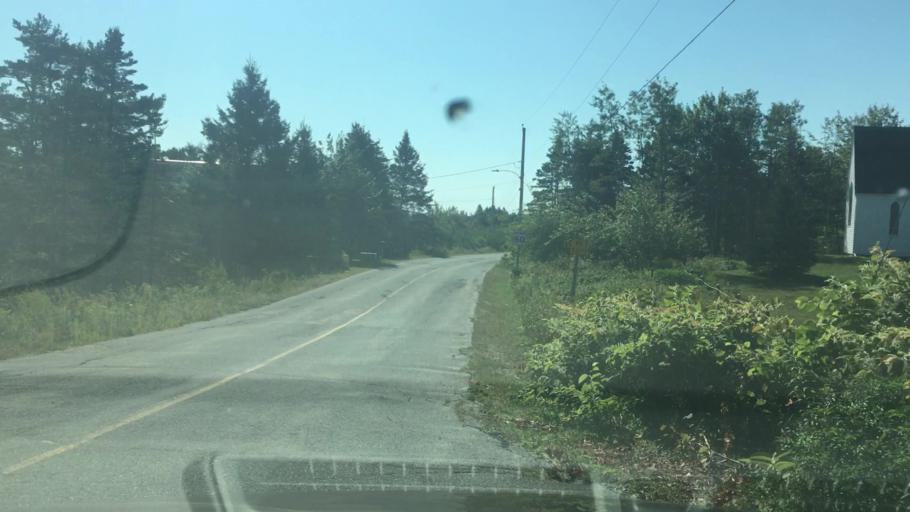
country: CA
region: Nova Scotia
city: New Glasgow
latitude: 44.8050
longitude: -62.6939
